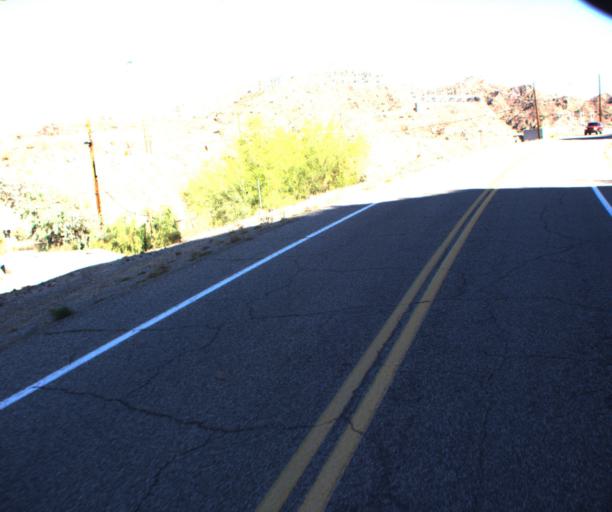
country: US
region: Arizona
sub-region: La Paz County
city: Cienega Springs
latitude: 34.2899
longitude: -114.1371
